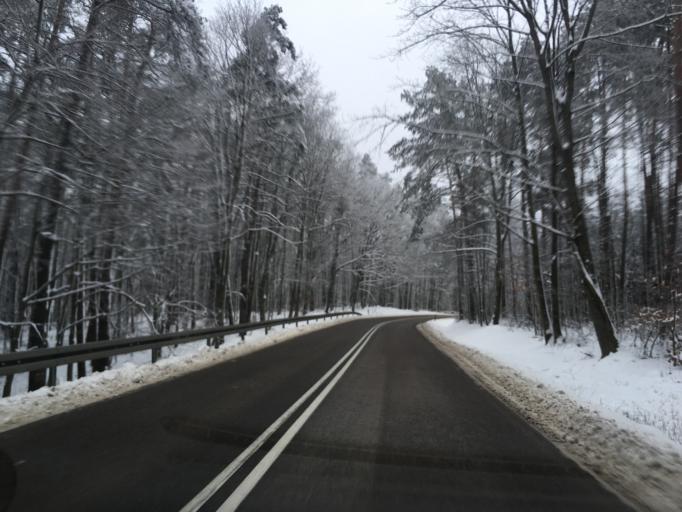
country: PL
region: Kujawsko-Pomorskie
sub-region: Powiat brodnicki
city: Gorzno
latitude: 53.2468
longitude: 19.7040
